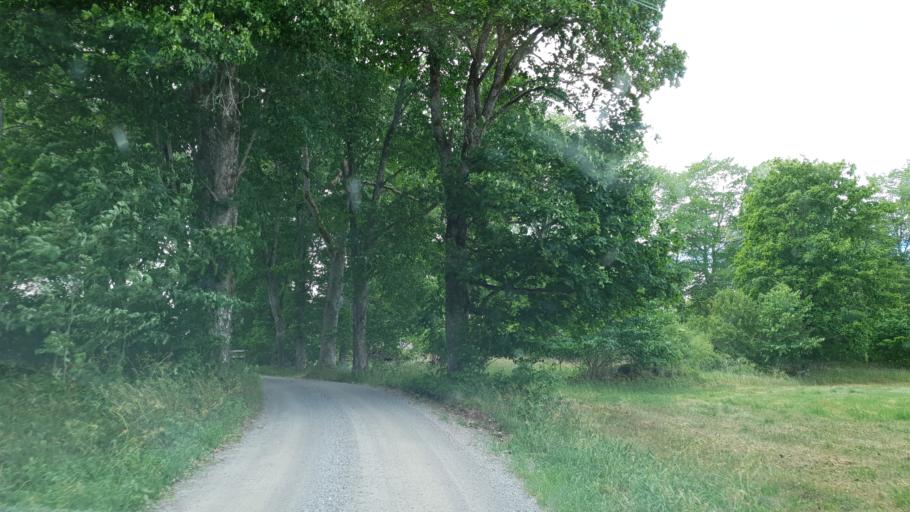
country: SE
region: Kalmar
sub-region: Hultsfreds Kommun
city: Virserum
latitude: 57.0922
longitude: 15.6253
